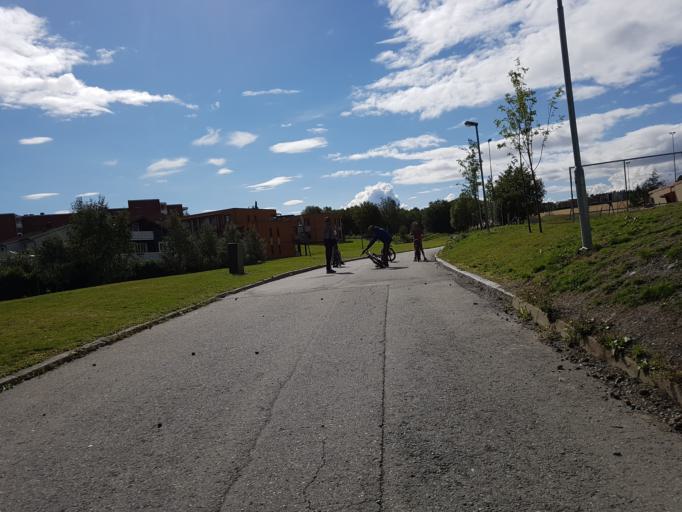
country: NO
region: Sor-Trondelag
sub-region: Trondheim
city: Trondheim
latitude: 63.4181
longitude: 10.4805
